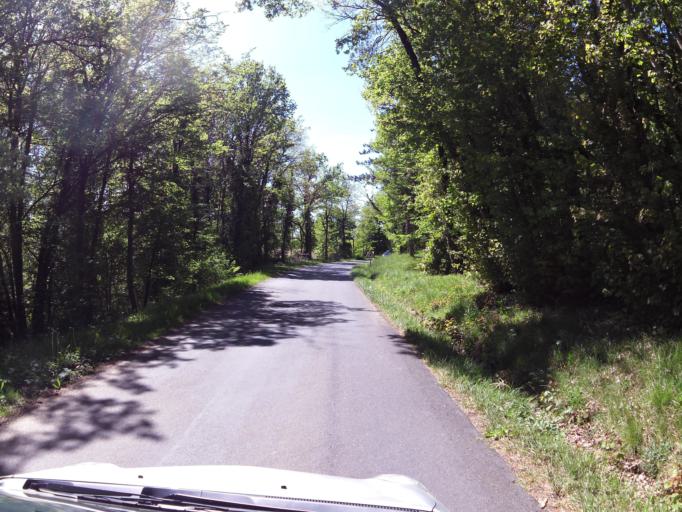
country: FR
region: Aquitaine
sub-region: Departement de la Dordogne
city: Sarlat-la-Caneda
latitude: 44.9224
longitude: 1.1628
